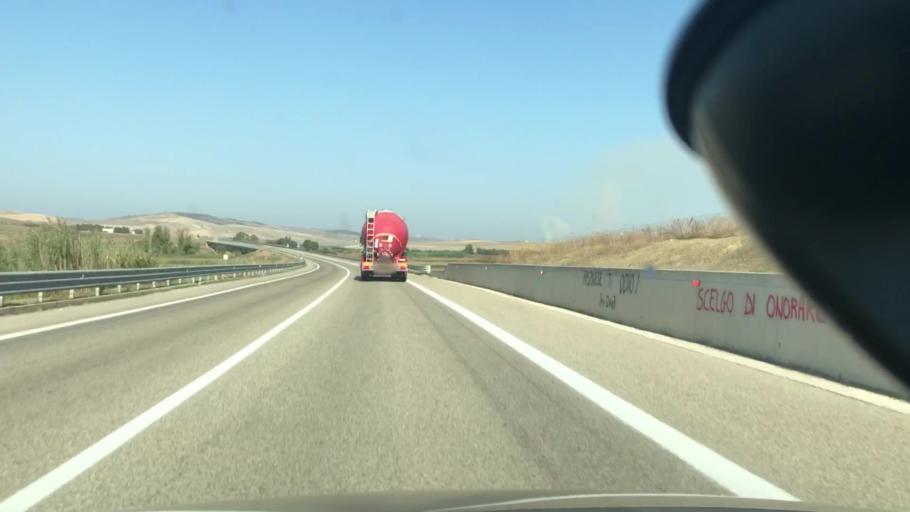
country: IT
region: Basilicate
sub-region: Provincia di Matera
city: Irsina
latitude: 40.7802
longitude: 16.3153
